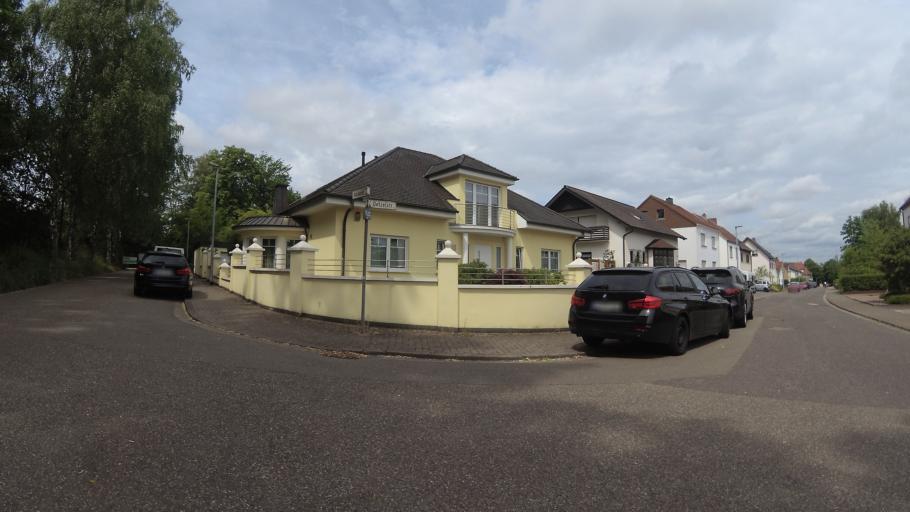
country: DE
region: Saarland
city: Sankt Ingbert
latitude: 49.2774
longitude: 7.1656
